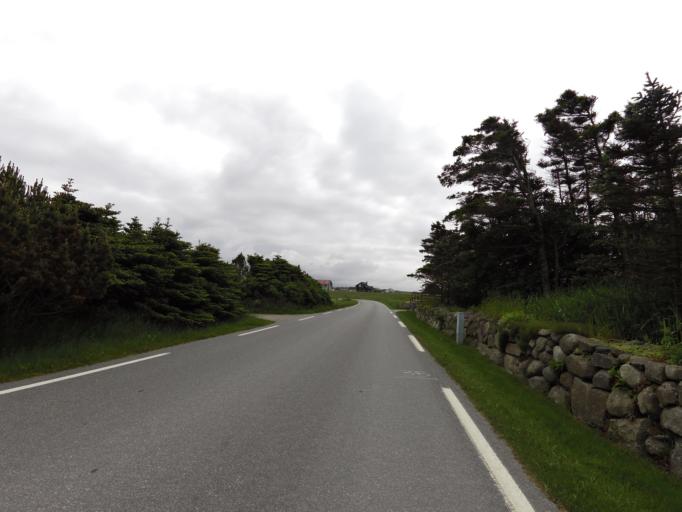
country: NO
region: Rogaland
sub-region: Klepp
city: Kleppe
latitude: 58.8122
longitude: 5.5528
